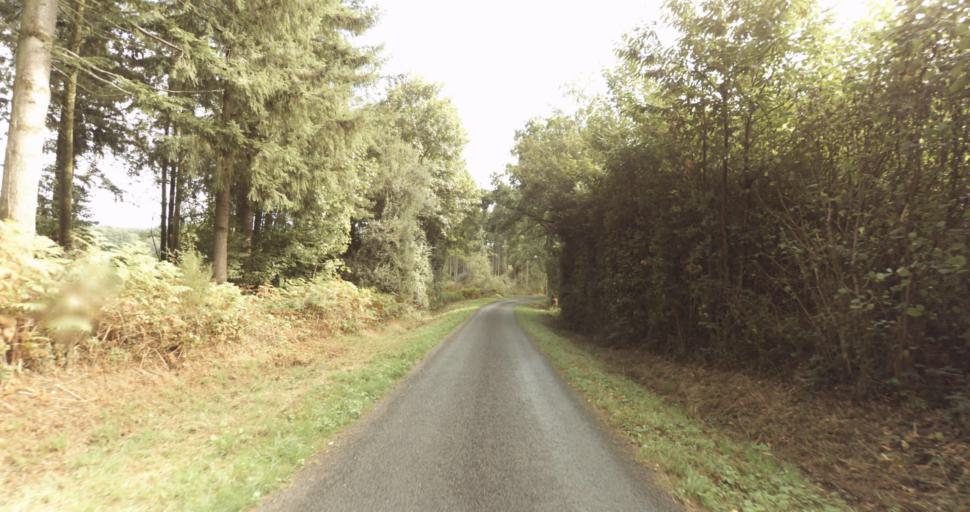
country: FR
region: Lower Normandy
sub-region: Departement de l'Orne
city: Sainte-Gauburge-Sainte-Colombe
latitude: 48.6738
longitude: 0.3825
